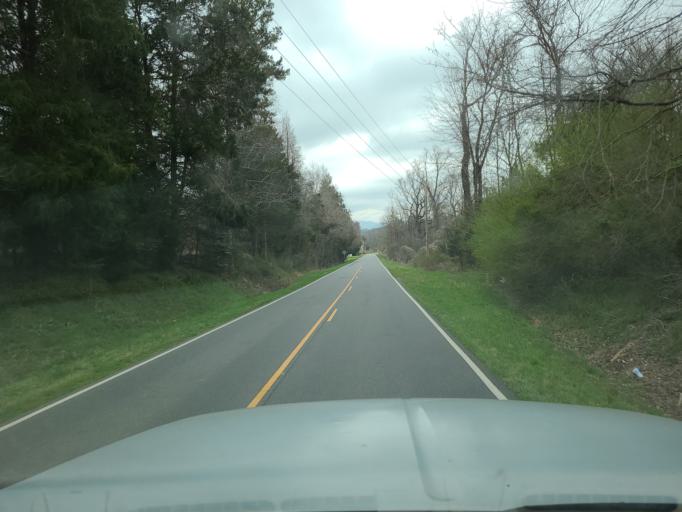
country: US
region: North Carolina
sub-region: Cleveland County
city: Shelby
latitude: 35.4425
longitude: -81.6438
